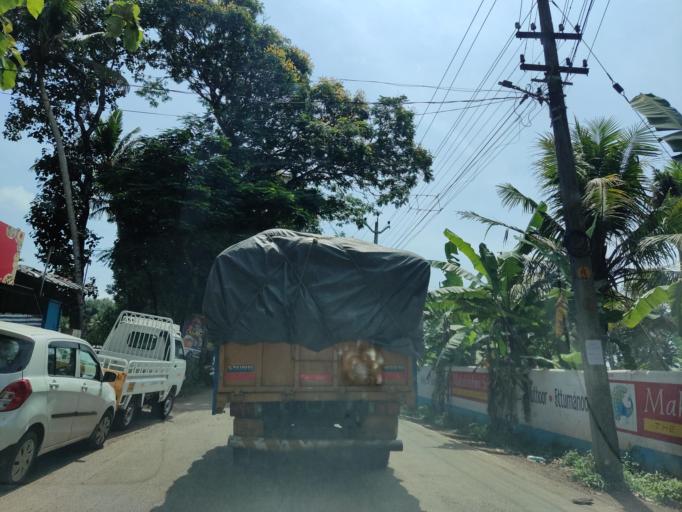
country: IN
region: Kerala
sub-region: Alappuzha
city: Chengannur
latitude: 9.3084
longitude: 76.5785
